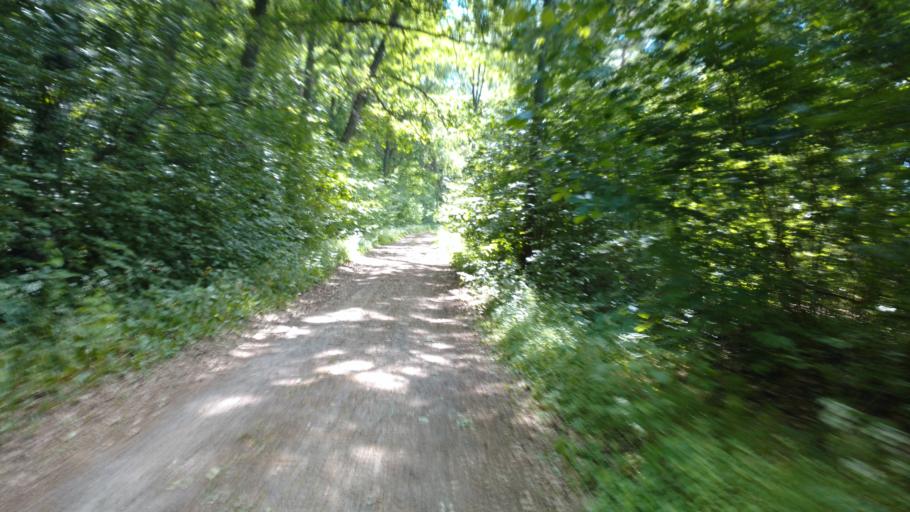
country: FI
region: Uusimaa
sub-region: Raaseporin
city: Pohja
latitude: 60.1107
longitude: 23.5473
